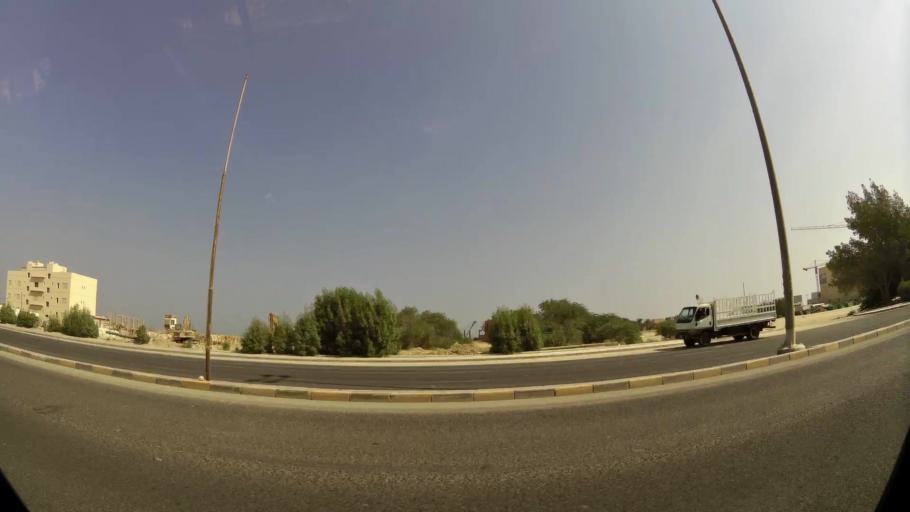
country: KW
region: Al Ahmadi
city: Al Mahbulah
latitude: 29.1252
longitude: 48.1332
